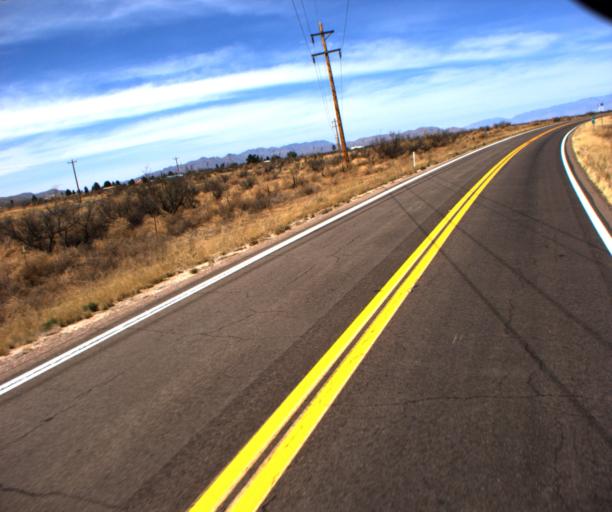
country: US
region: Arizona
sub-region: Cochise County
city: Willcox
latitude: 32.1066
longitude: -109.9140
